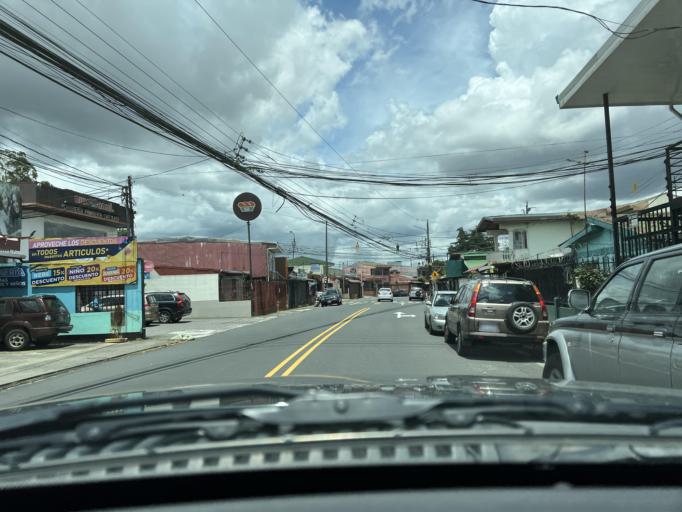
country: CR
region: San Jose
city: Sabanilla
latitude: 9.9411
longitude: -84.0277
